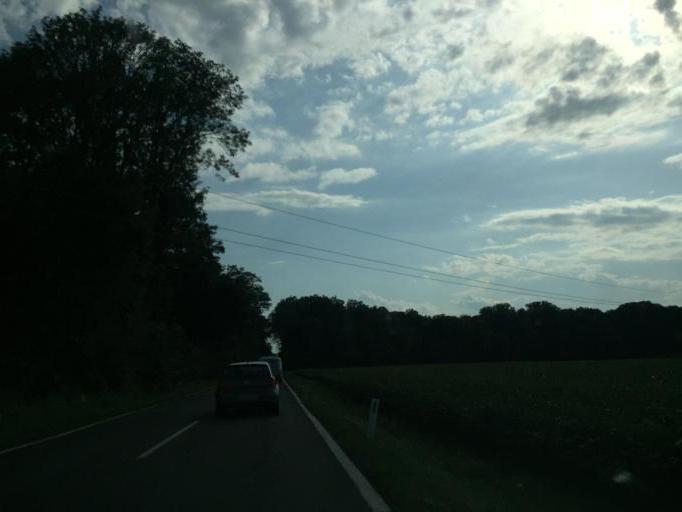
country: AT
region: Styria
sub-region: Politischer Bezirk Suedoststeiermark
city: Deutsch Goritz
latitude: 46.7346
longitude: 15.8646
